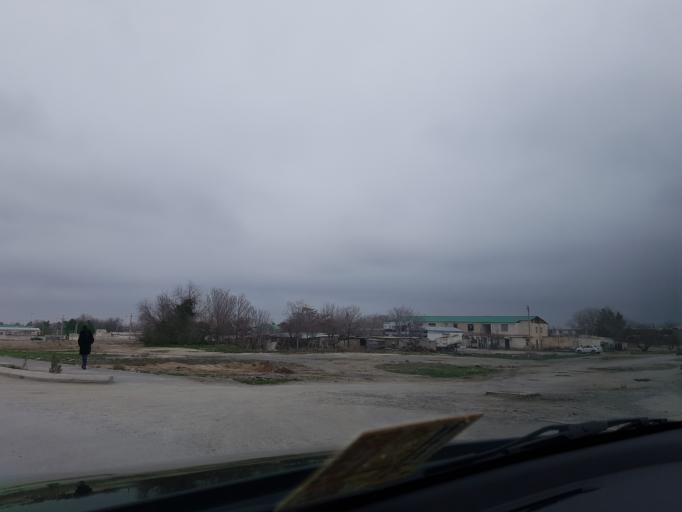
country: TM
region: Ahal
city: Abadan
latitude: 38.1446
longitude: 57.9529
